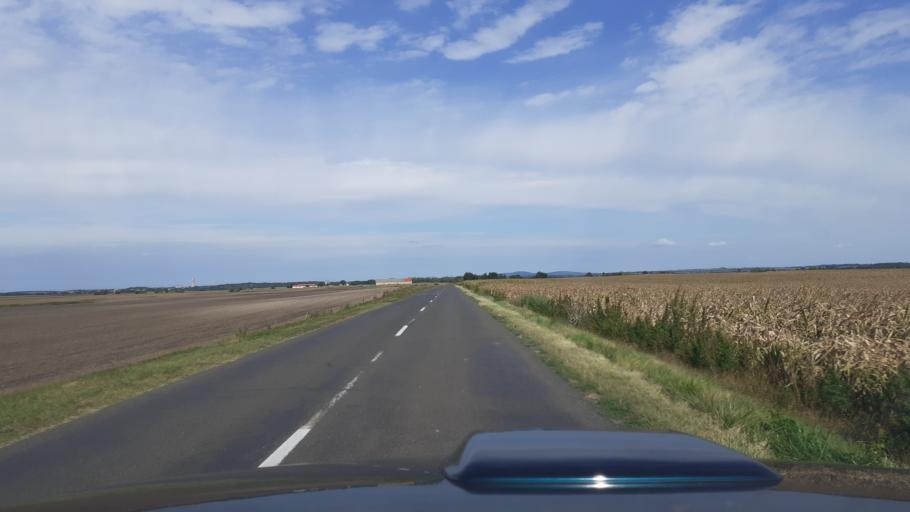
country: HU
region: Fejer
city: Pusztaszabolcs
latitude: 47.1087
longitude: 18.7058
